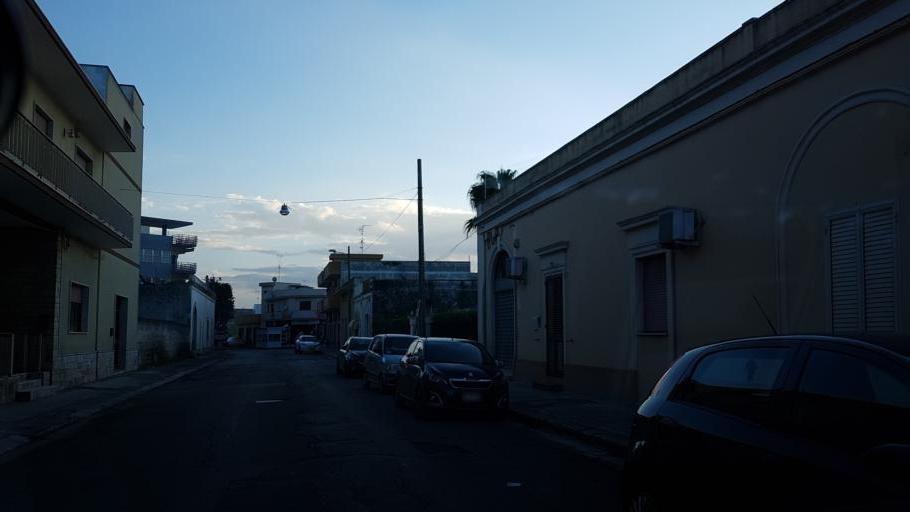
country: IT
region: Apulia
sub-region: Provincia di Lecce
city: Surbo
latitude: 40.3939
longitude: 18.1297
